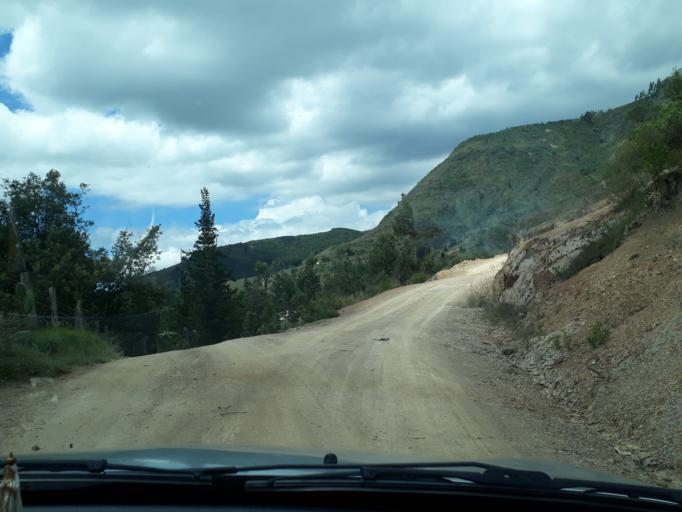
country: CO
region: Boyaca
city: Floresta
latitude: 5.8526
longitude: -72.9508
